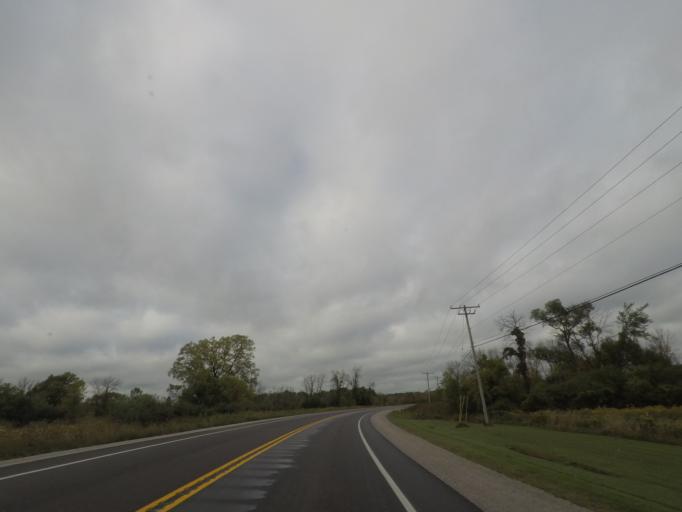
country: US
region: Wisconsin
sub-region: Jefferson County
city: Jefferson
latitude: 43.0129
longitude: -88.7523
